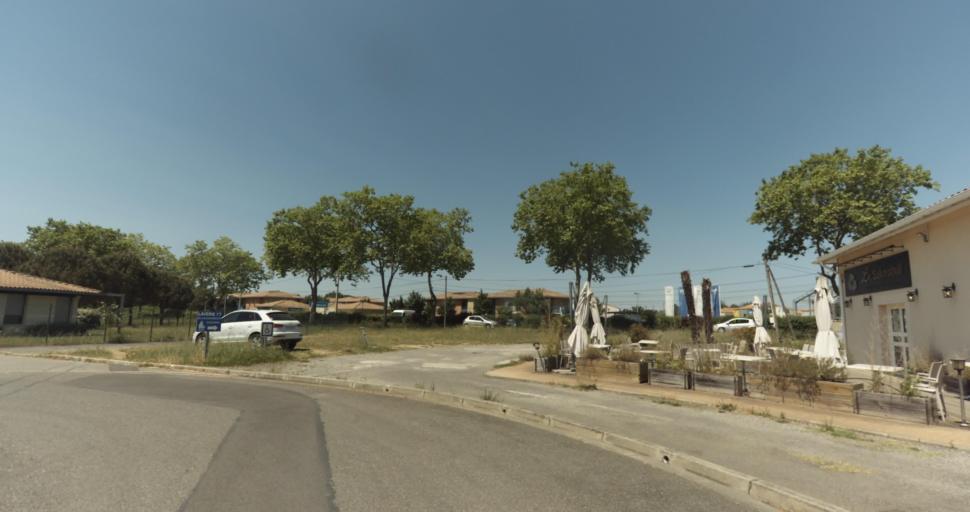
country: FR
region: Midi-Pyrenees
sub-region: Departement de la Haute-Garonne
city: Brax
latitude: 43.6020
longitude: 1.2571
